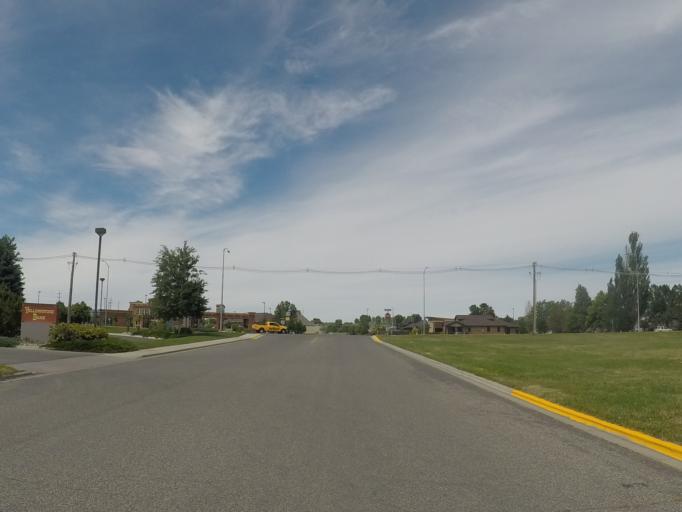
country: US
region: Montana
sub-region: Yellowstone County
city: Billings
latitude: 45.7857
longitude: -108.6164
